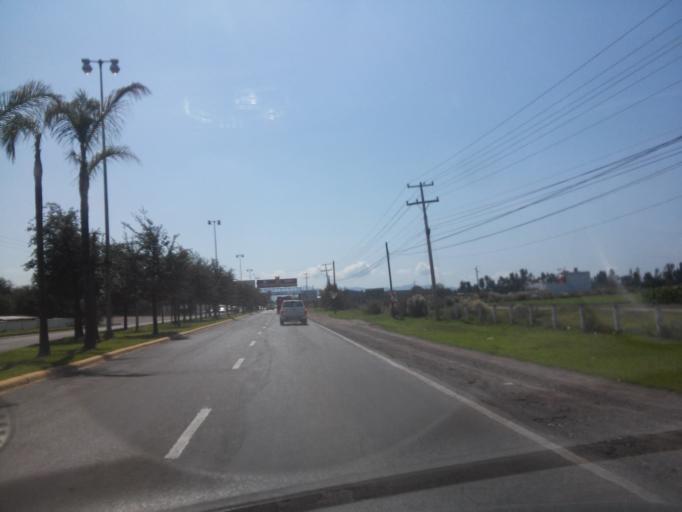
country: MX
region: Durango
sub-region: Durango
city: Sebastian Lerdo de Tejada
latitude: 23.9902
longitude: -104.6207
